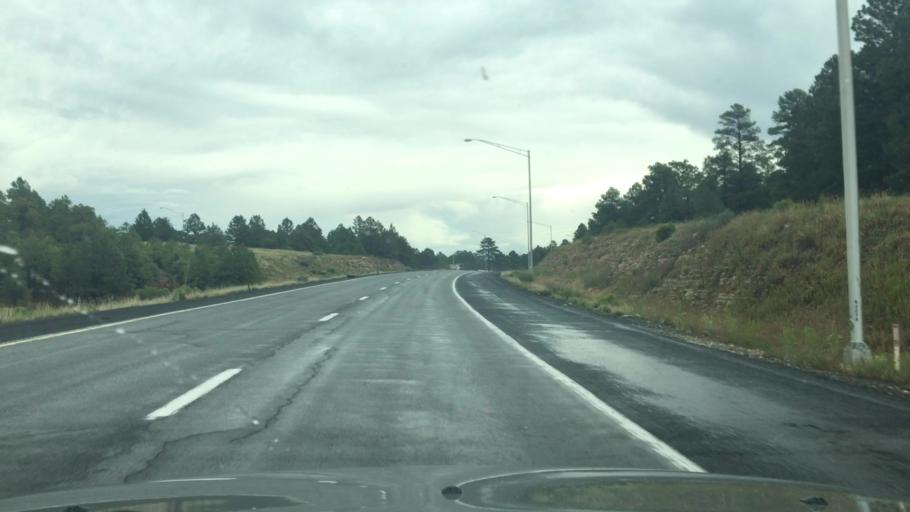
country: US
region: Arizona
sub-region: Coconino County
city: Flagstaff
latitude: 35.1702
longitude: -111.6624
